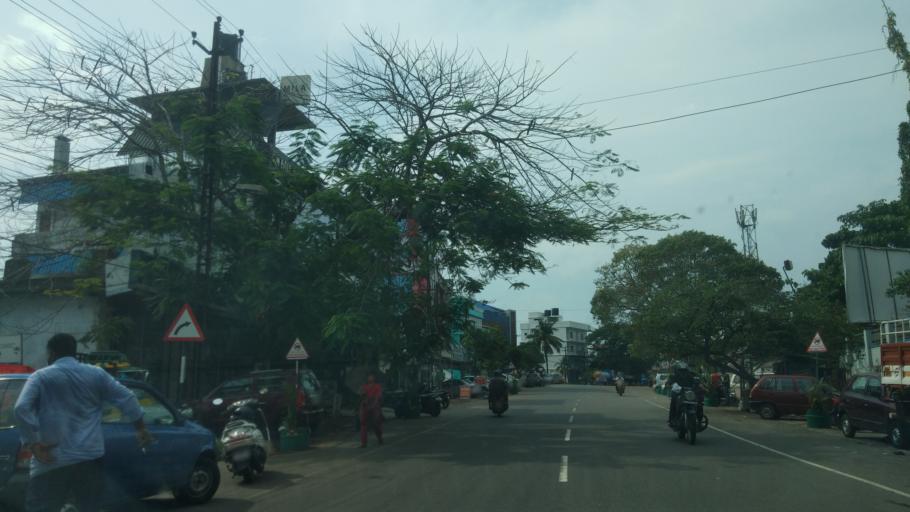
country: IN
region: Kerala
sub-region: Ernakulam
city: Elur
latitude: 10.0631
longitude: 76.3225
